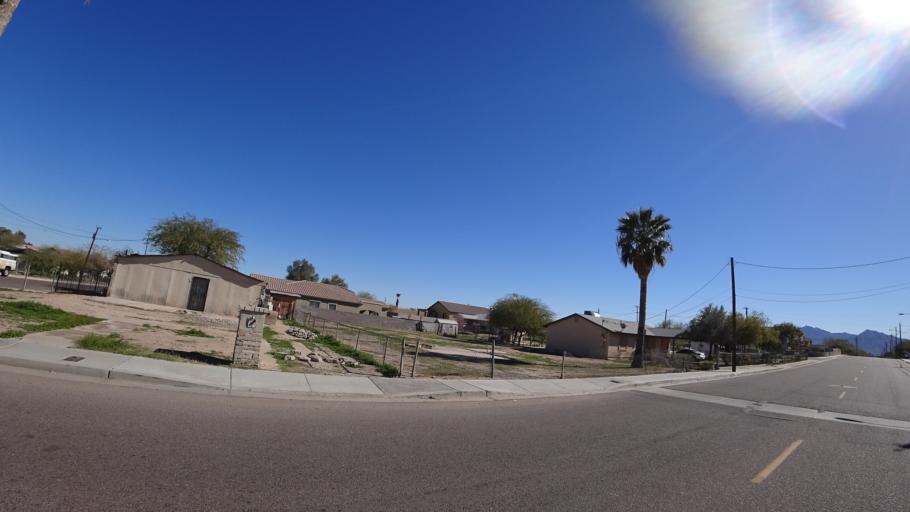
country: US
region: Arizona
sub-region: Maricopa County
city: Avondale
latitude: 33.4297
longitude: -112.3452
